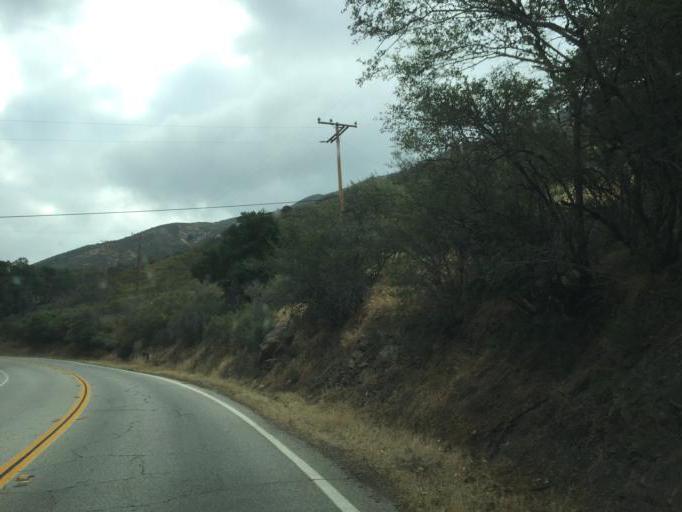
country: US
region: California
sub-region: Los Angeles County
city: Green Valley
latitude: 34.5600
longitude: -118.4041
